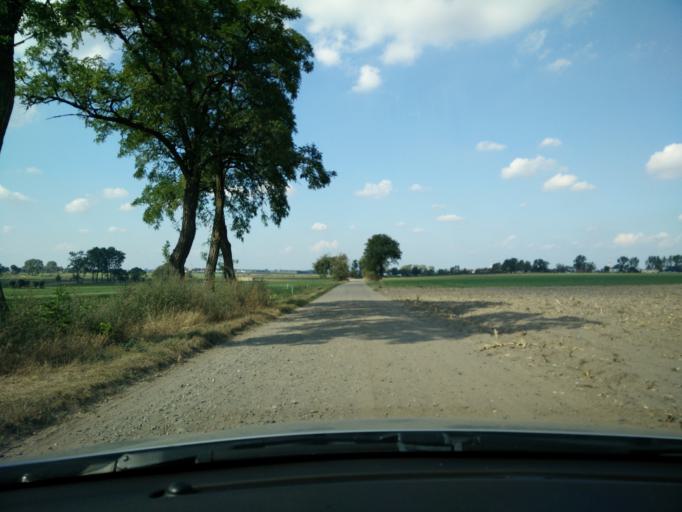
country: PL
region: Greater Poland Voivodeship
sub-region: Powiat poznanski
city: Kleszczewo
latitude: 52.2622
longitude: 17.1828
